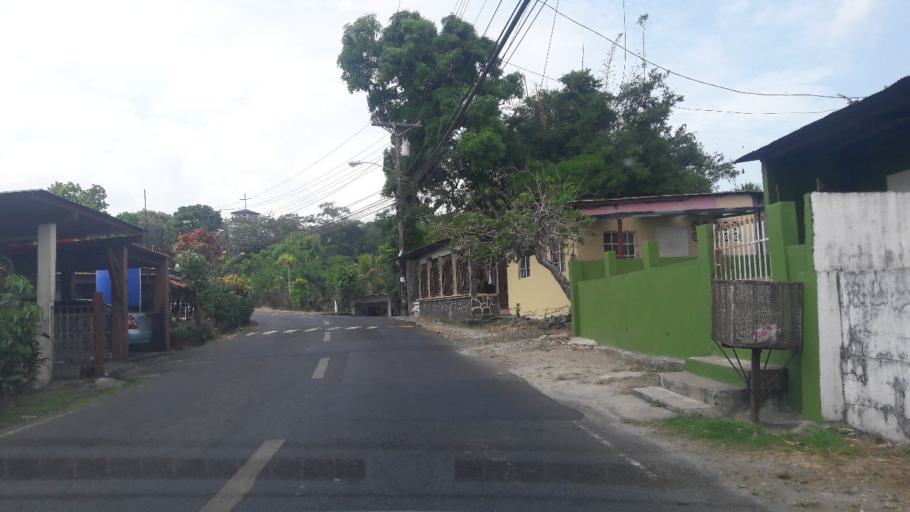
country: PA
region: Panama
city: Alcalde Diaz
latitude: 9.1204
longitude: -79.5564
